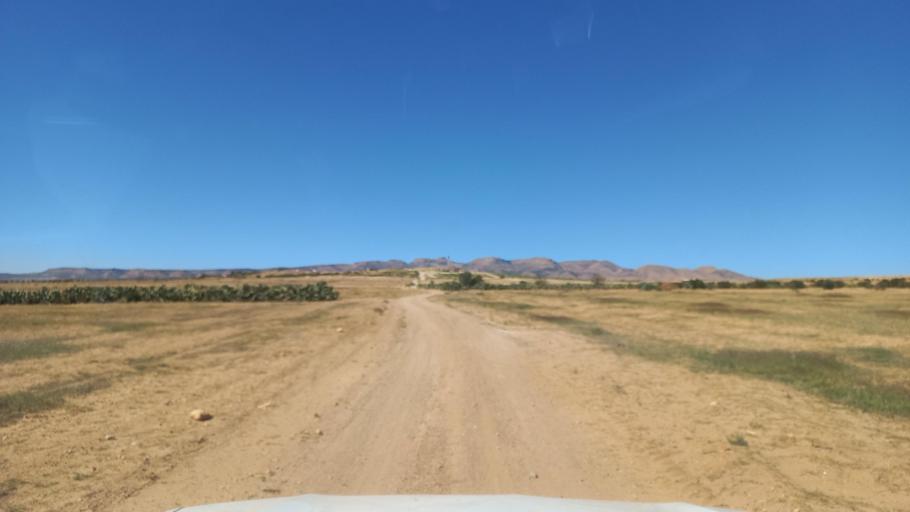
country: TN
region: Al Qasrayn
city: Sbiba
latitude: 35.3708
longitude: 9.0839
